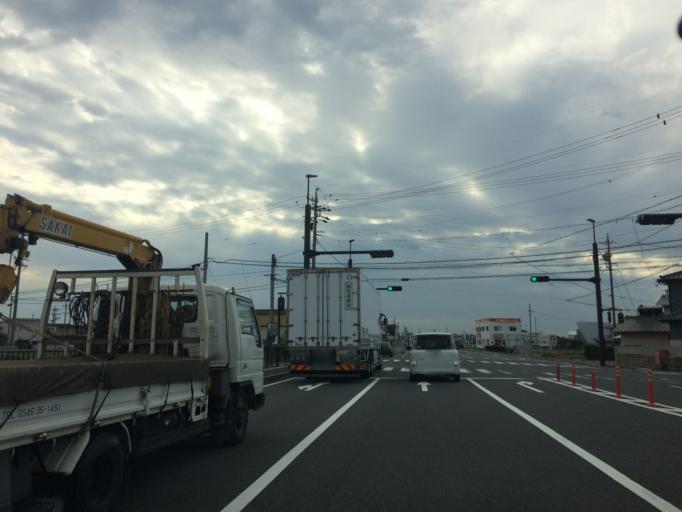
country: JP
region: Shizuoka
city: Shimada
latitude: 34.7827
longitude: 138.2496
